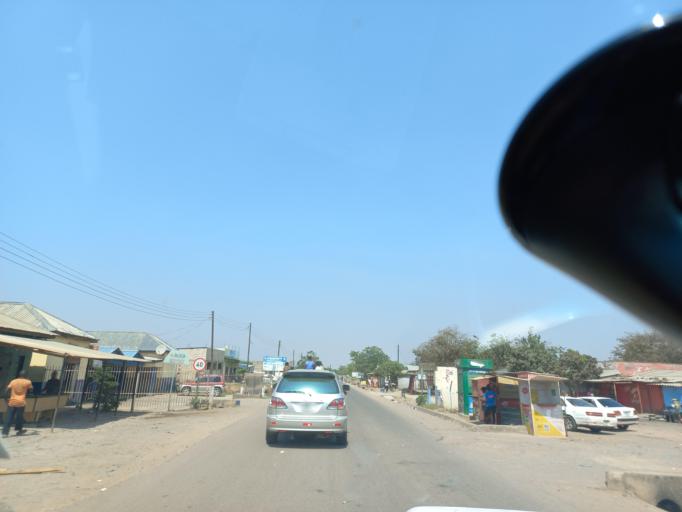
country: ZM
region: Lusaka
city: Kafue
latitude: -15.7467
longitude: 28.1853
